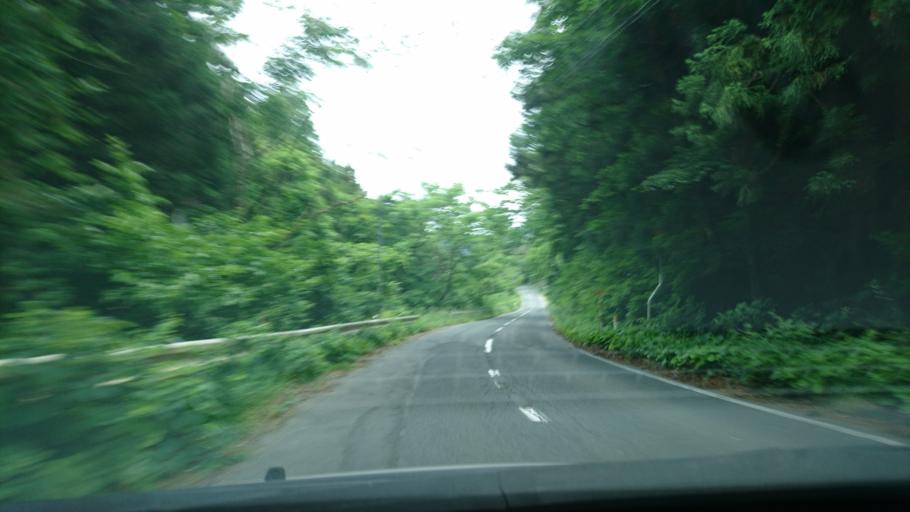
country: JP
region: Iwate
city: Ichinoseki
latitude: 38.9479
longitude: 141.2664
